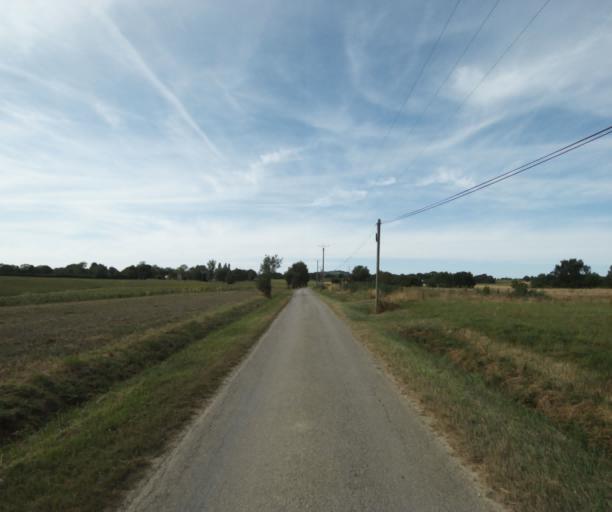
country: FR
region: Midi-Pyrenees
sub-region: Departement du Tarn
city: Puylaurens
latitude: 43.5345
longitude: 2.0534
